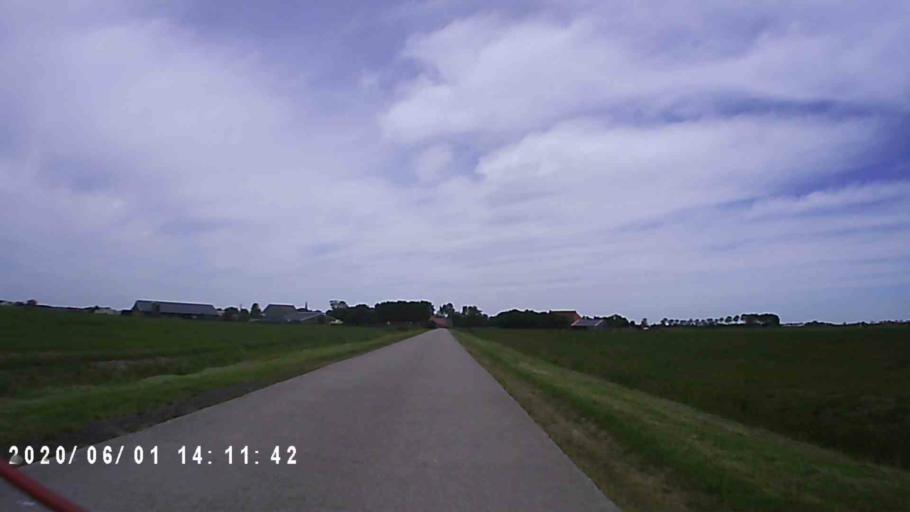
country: NL
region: Friesland
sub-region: Gemeente Littenseradiel
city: Winsum
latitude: 53.1278
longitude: 5.6497
